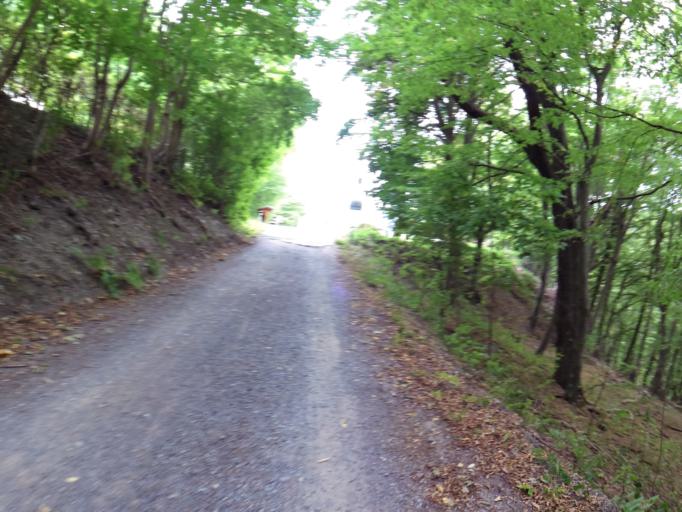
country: DE
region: North Rhine-Westphalia
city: Heimbach
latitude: 50.6056
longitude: 6.4203
